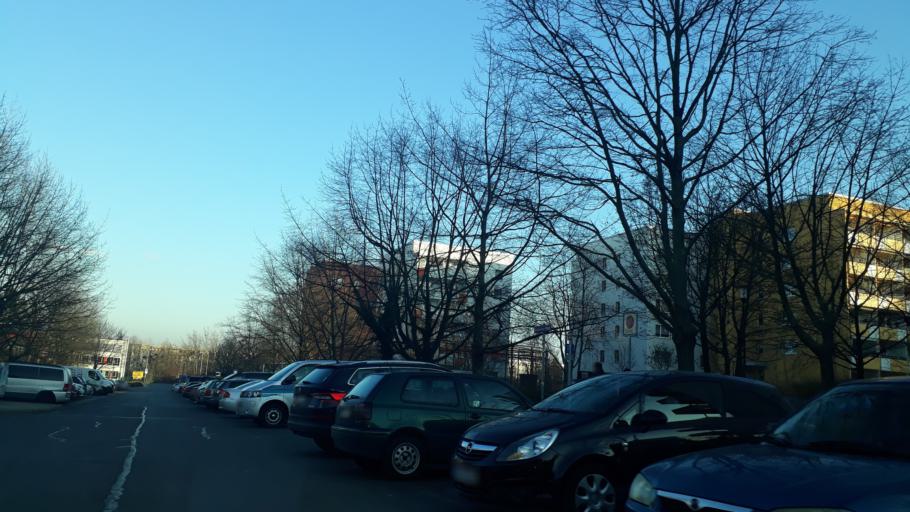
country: DE
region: Saxony
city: Freital
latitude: 51.0460
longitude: 13.6752
